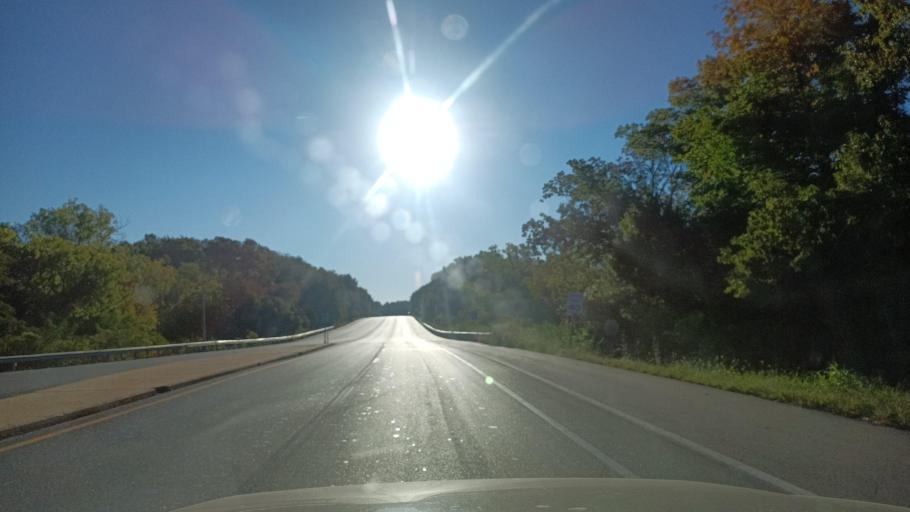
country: US
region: Missouri
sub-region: Boone County
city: Columbia
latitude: 38.9344
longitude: -92.3222
